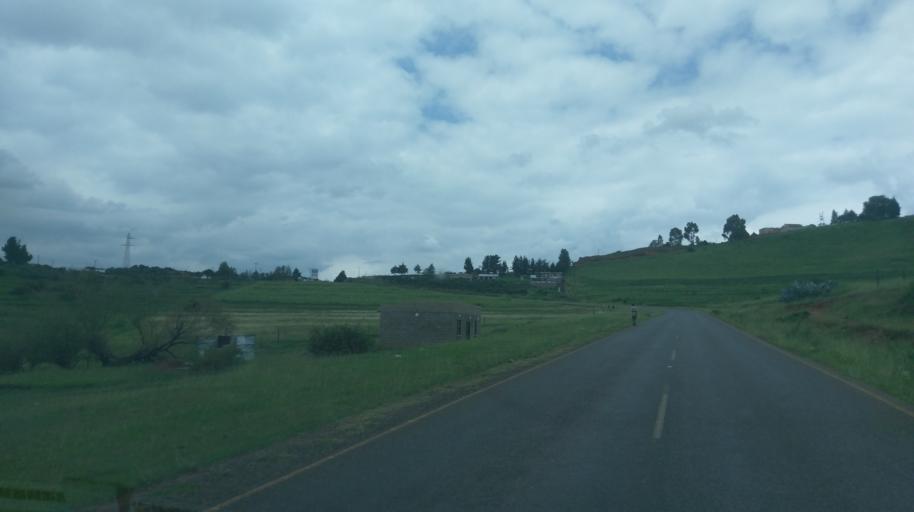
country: LS
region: Leribe
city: Leribe
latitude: -28.9962
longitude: 28.1991
